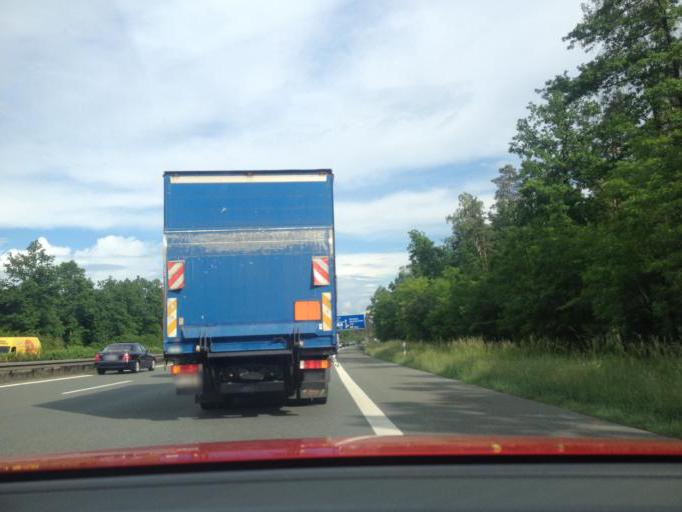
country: DE
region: Bavaria
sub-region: Regierungsbezirk Mittelfranken
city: Schwaig
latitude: 49.4838
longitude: 11.1676
